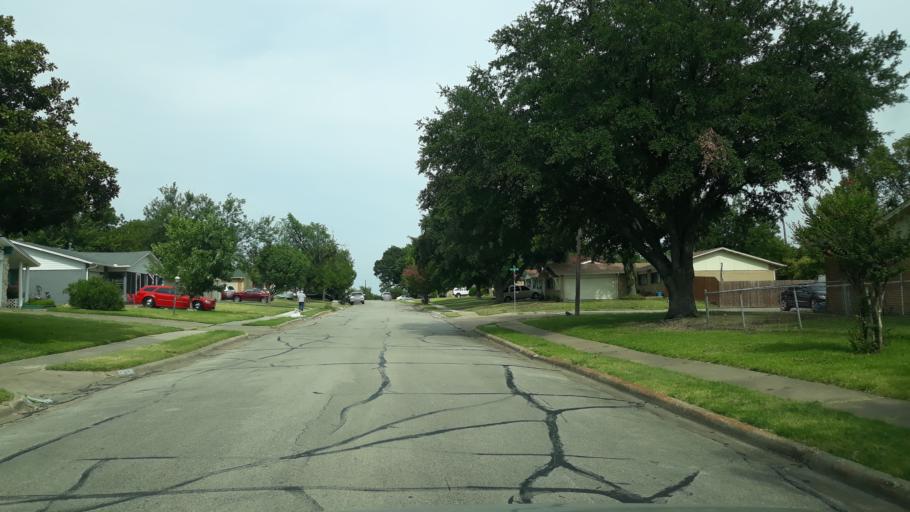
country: US
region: Texas
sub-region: Dallas County
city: Irving
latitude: 32.8486
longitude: -96.9851
